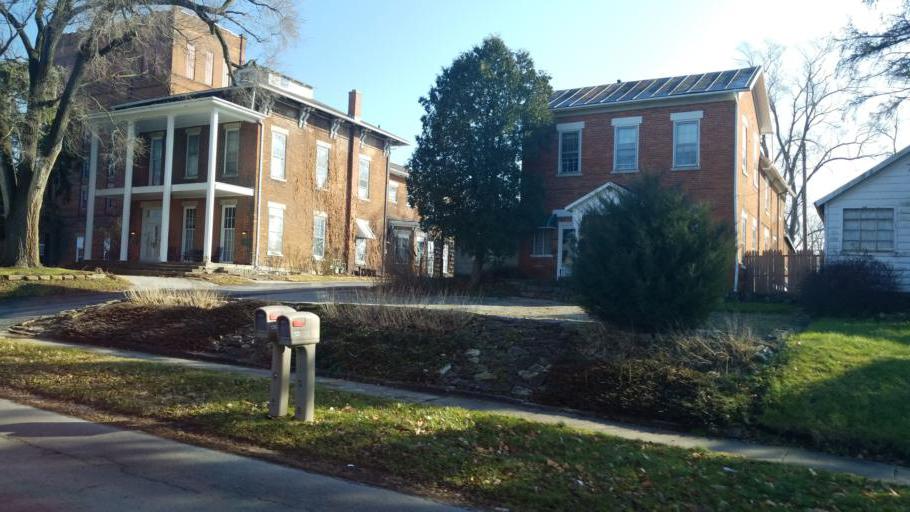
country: US
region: Ohio
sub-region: Seneca County
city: Tiffin
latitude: 41.1194
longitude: -83.1737
